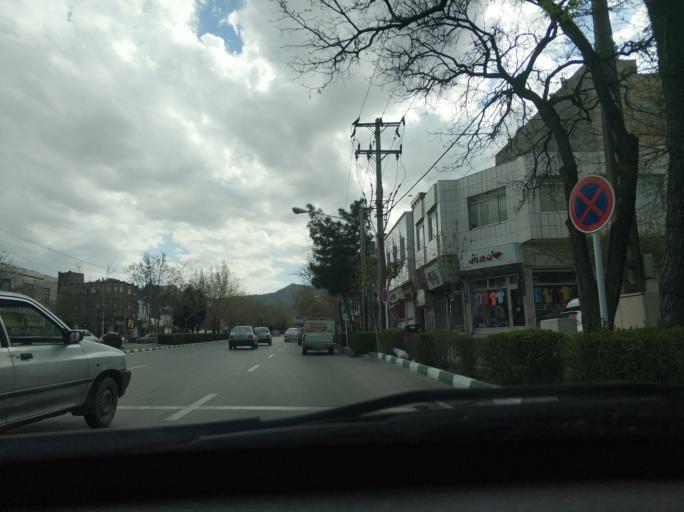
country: IR
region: Razavi Khorasan
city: Mashhad
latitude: 36.2673
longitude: 59.5870
